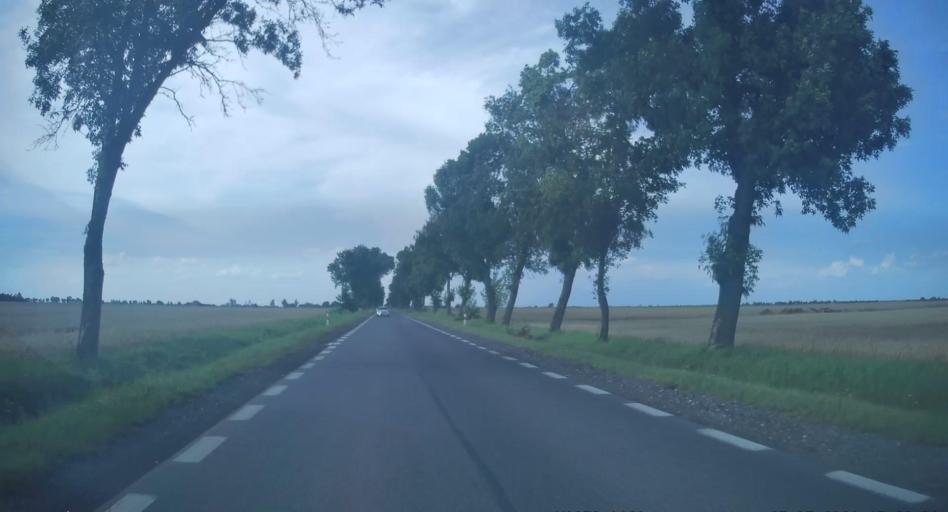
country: PL
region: Lodz Voivodeship
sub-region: Powiat tomaszowski
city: Rzeczyca
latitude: 51.6190
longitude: 20.2929
